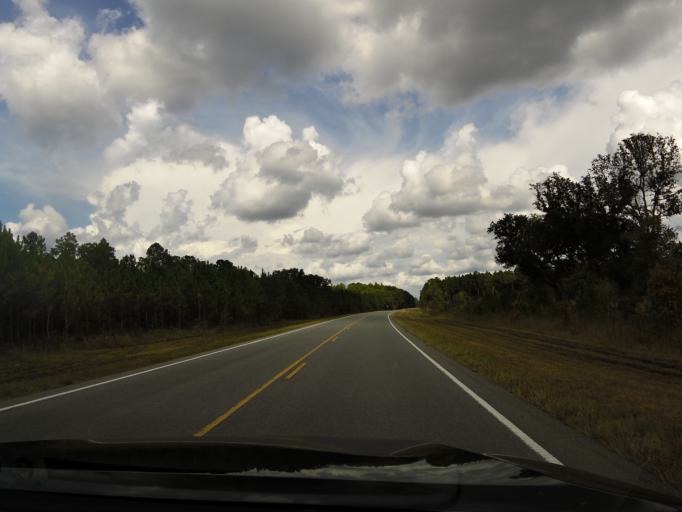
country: US
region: Georgia
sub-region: Charlton County
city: Folkston
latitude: 31.0061
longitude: -82.0271
